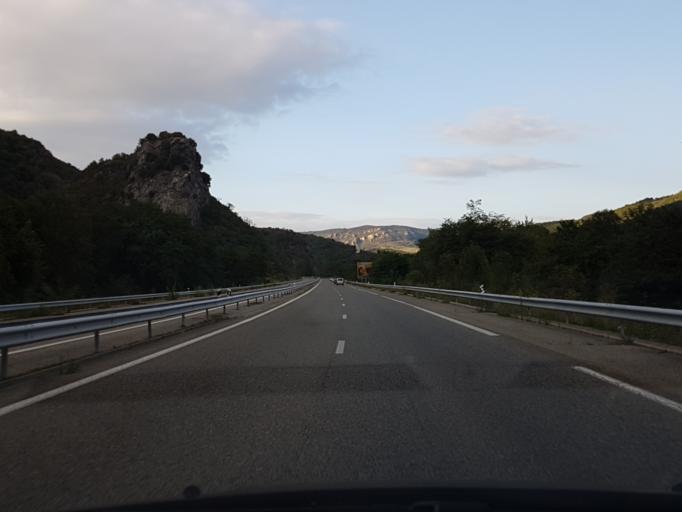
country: FR
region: Midi-Pyrenees
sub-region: Departement de l'Ariege
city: Mercus-Garrabet
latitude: 42.8888
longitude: 1.6277
